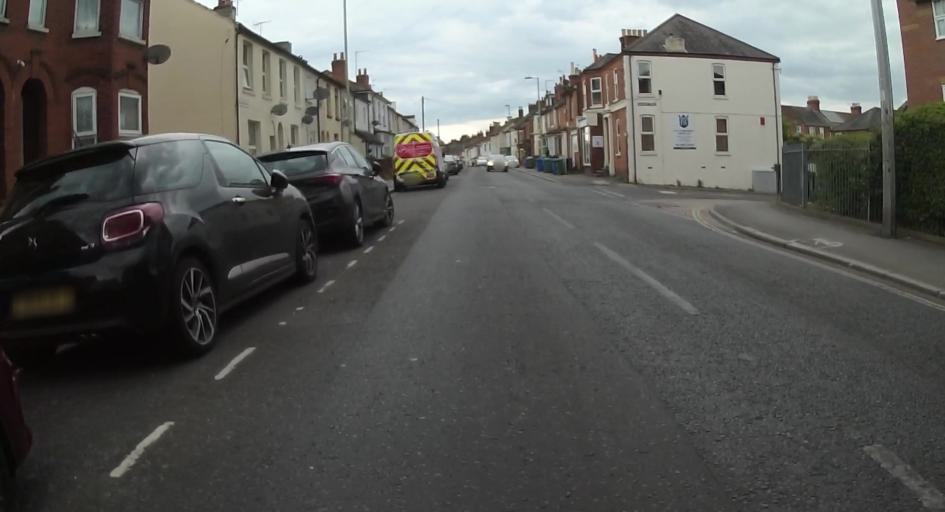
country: GB
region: England
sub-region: Hampshire
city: Aldershot
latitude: 51.2452
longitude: -0.7655
